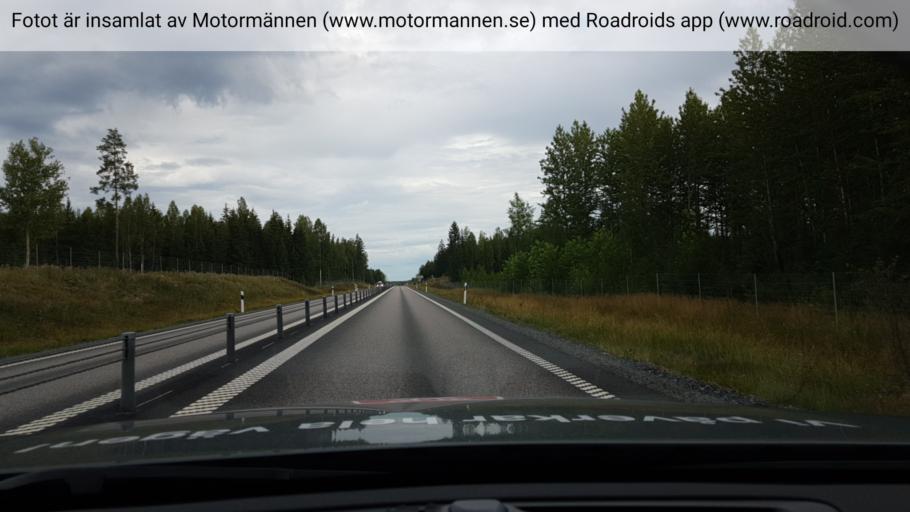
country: SE
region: Uppsala
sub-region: Heby Kommun
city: Heby
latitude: 59.9836
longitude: 16.8533
